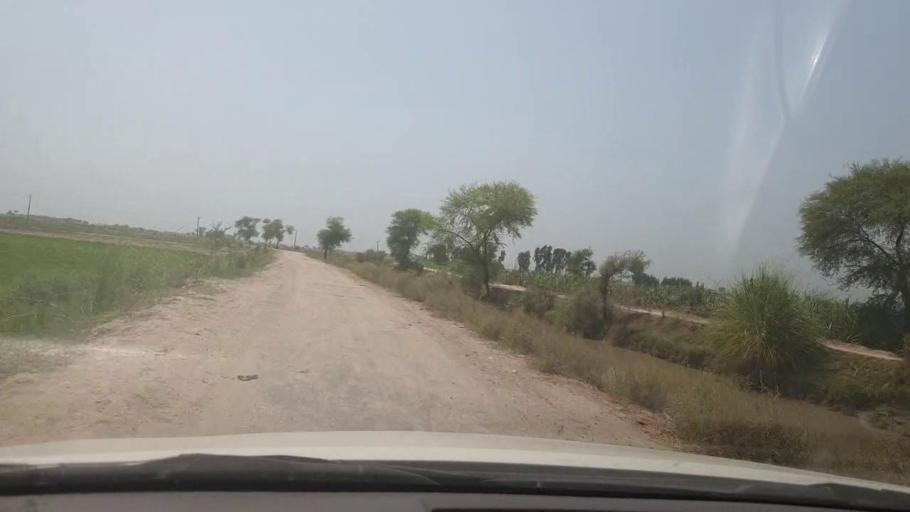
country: PK
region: Sindh
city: Shikarpur
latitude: 28.0513
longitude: 68.5875
